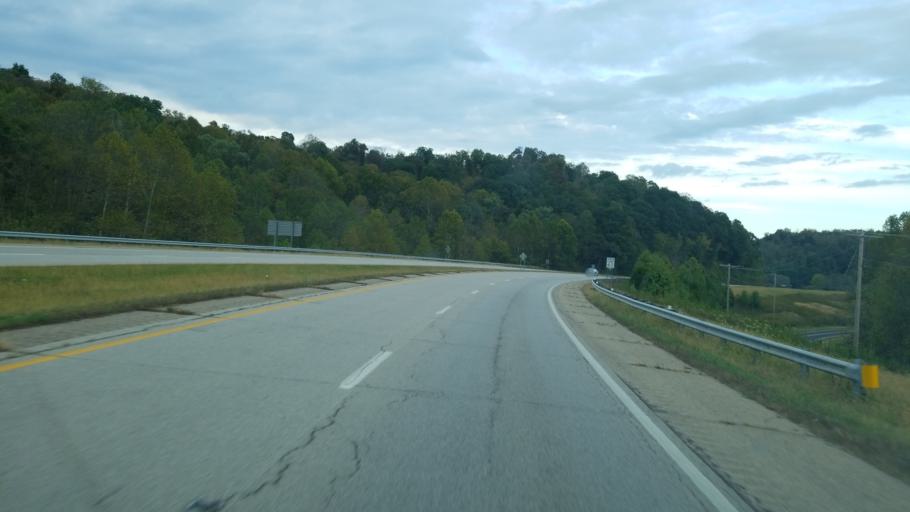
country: US
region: Ohio
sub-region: Meigs County
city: Pomeroy
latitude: 39.0464
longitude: -82.0517
